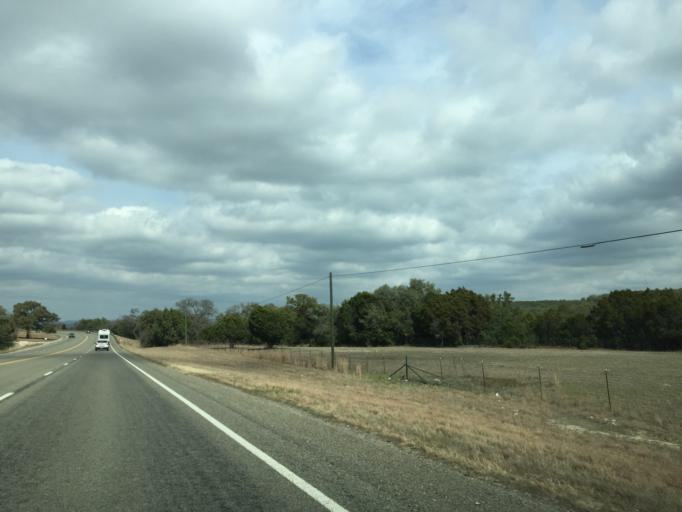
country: US
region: Texas
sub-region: Travis County
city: Briarcliff
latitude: 30.4483
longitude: -98.1483
